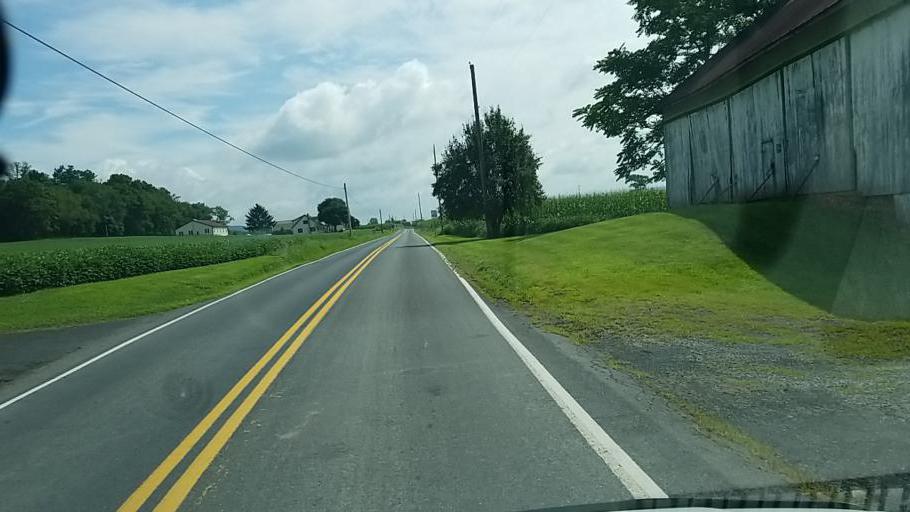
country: US
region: Pennsylvania
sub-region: Dauphin County
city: Millersburg
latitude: 40.5872
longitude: -76.9122
